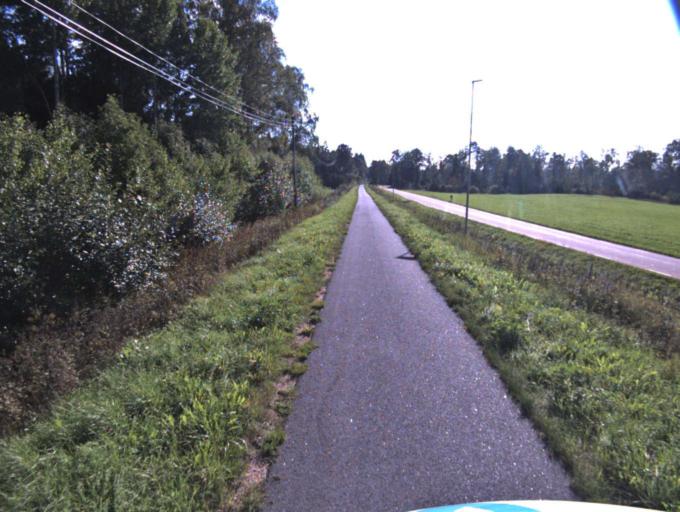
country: SE
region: Vaestra Goetaland
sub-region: Boras Kommun
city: Dalsjofors
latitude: 57.8223
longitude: 13.1557
